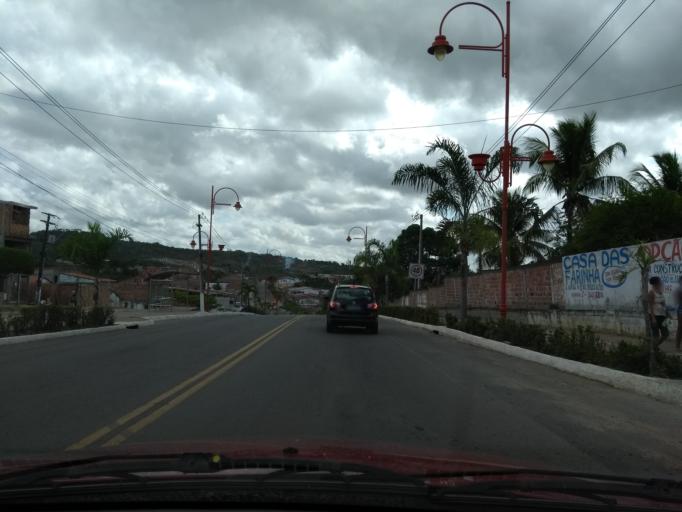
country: BR
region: Bahia
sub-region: Sao Francisco Do Conde
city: Sao Francisco do Conde
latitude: -12.6200
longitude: -38.6702
